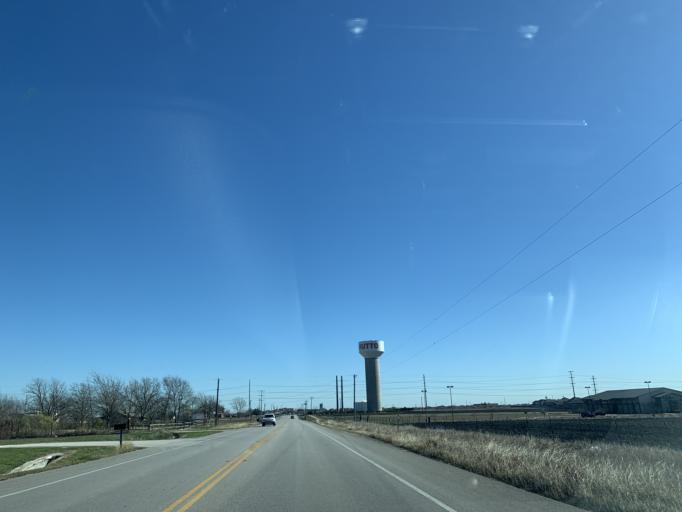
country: US
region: Texas
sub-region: Williamson County
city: Hutto
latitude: 30.5581
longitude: -97.5652
